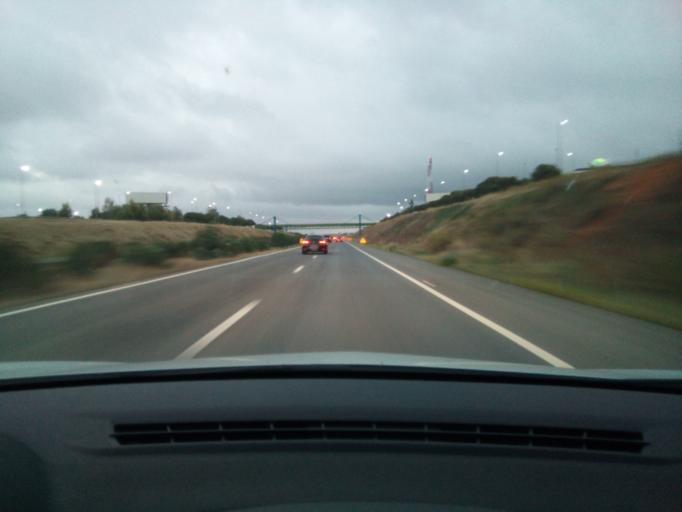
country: MA
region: Meknes-Tafilalet
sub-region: Meknes
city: Meknes
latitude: 33.8325
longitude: -5.5721
